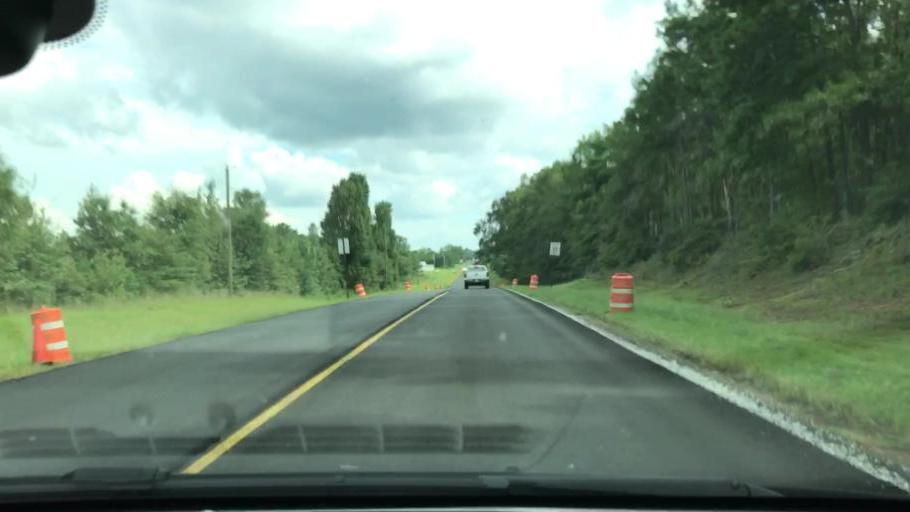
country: US
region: Georgia
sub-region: Clay County
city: Fort Gaines
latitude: 31.5850
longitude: -85.0276
